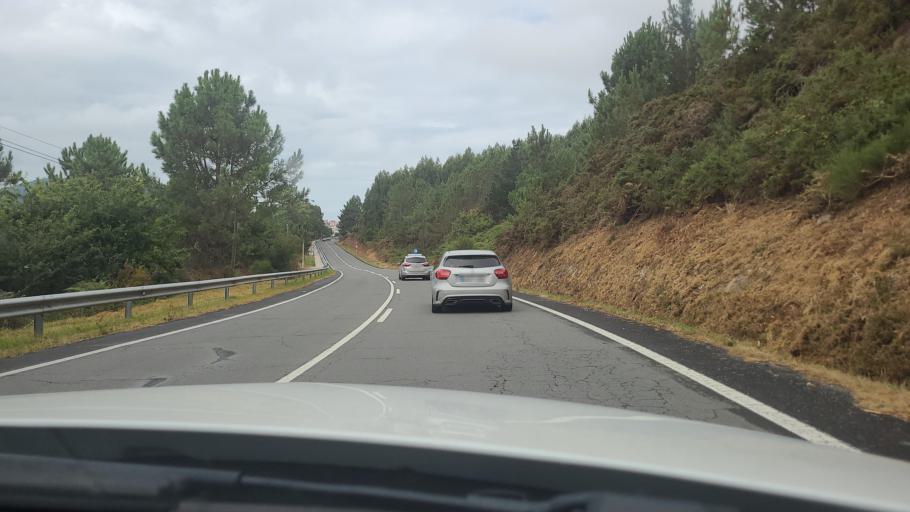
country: ES
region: Galicia
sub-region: Provincia da Coruna
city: Fisterra
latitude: 42.9297
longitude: -9.2416
